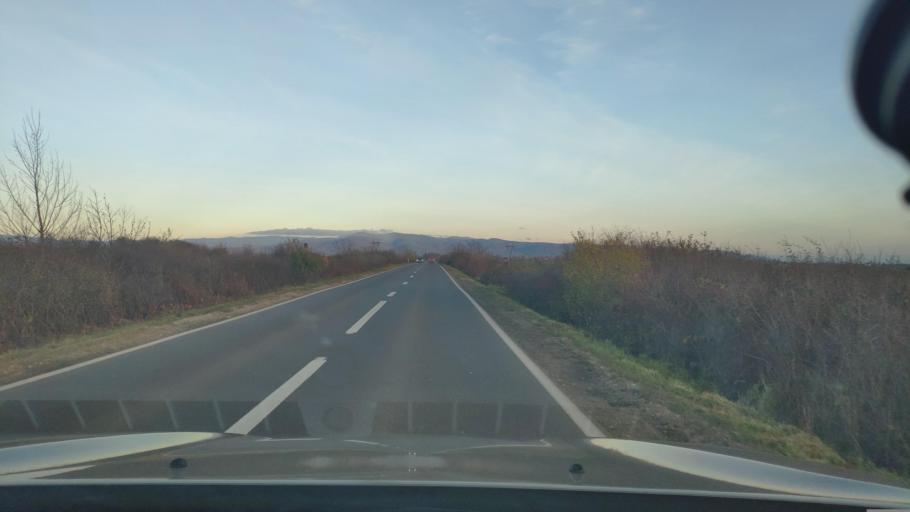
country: RO
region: Satu Mare
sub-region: Comuna Mediesu Aurit
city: Mediesu Aurit
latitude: 47.7672
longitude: 23.1623
